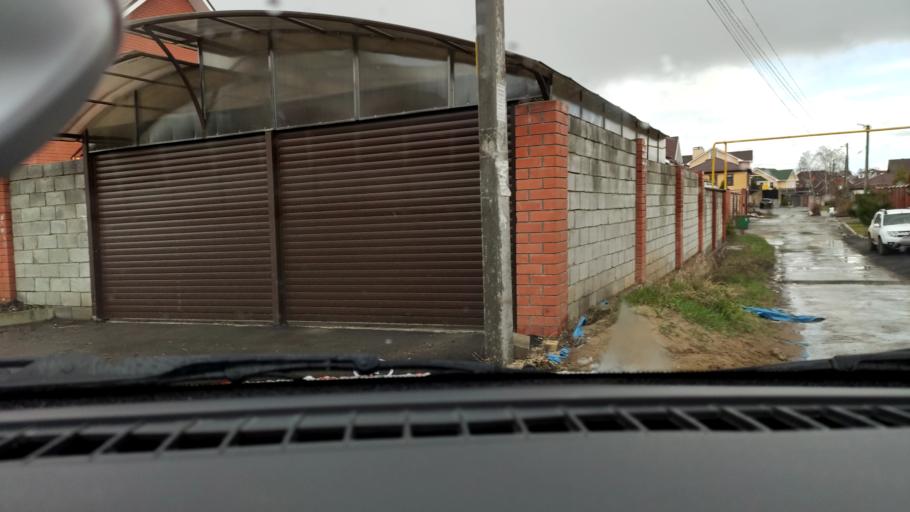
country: RU
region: Samara
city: Novosemeykino
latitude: 53.3303
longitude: 50.2867
